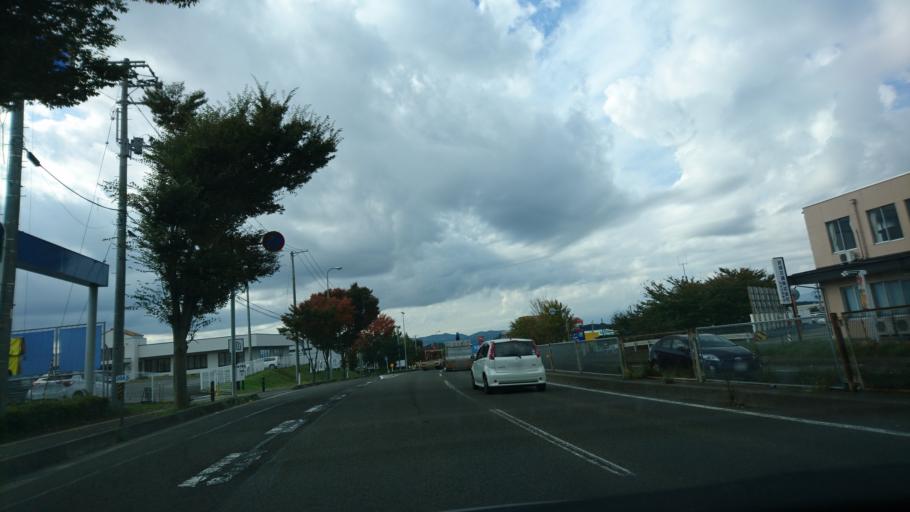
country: JP
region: Miyagi
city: Tomiya
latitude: 38.3587
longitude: 140.8732
